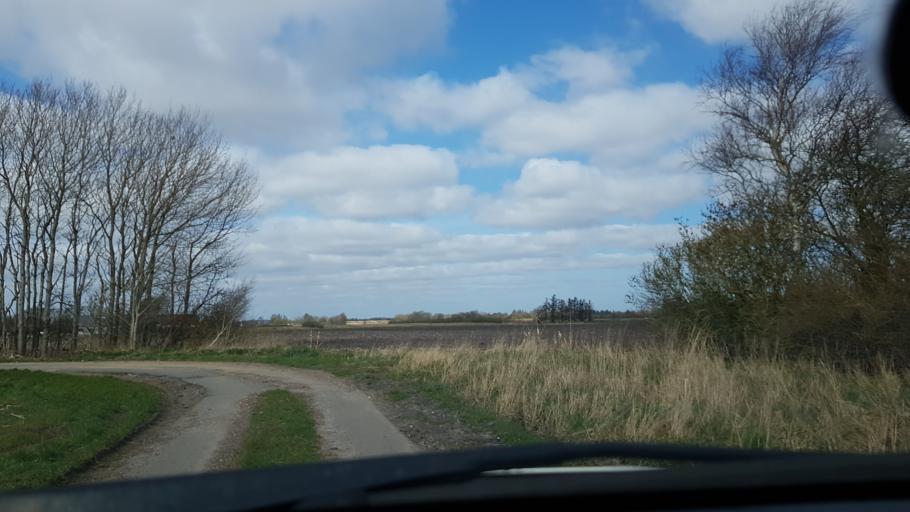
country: DK
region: South Denmark
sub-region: Esbjerg Kommune
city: Ribe
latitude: 55.2543
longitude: 8.8388
